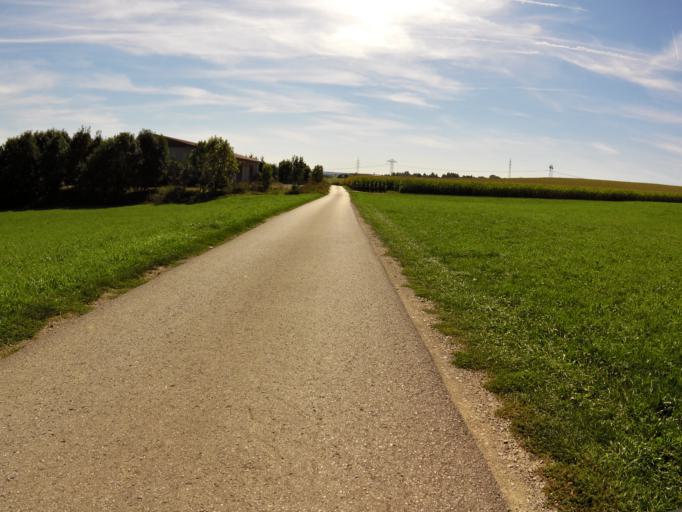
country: DE
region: Baden-Wuerttemberg
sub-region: Freiburg Region
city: Donaueschingen
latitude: 47.9758
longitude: 8.5050
